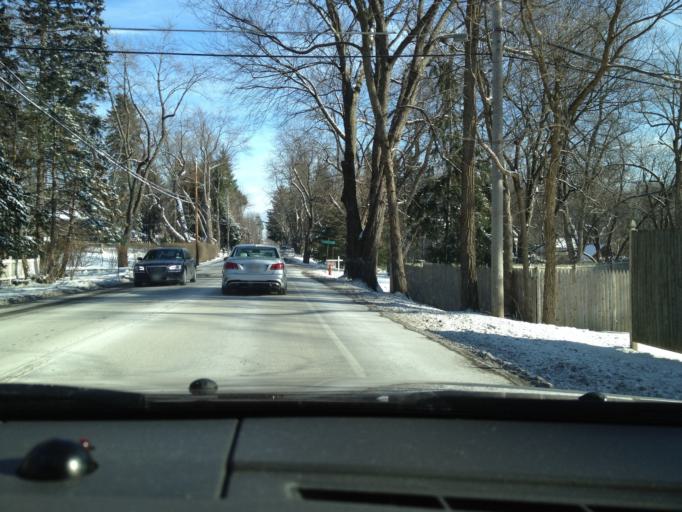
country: US
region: New York
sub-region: Albany County
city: West Albany
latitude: 42.7064
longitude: -73.7640
